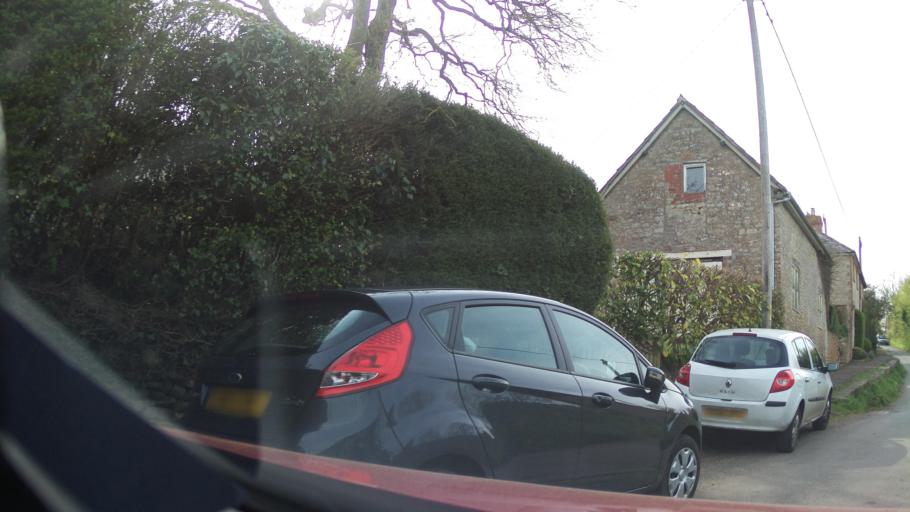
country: GB
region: England
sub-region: Dorset
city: Sherborne
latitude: 50.9790
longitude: -2.5007
